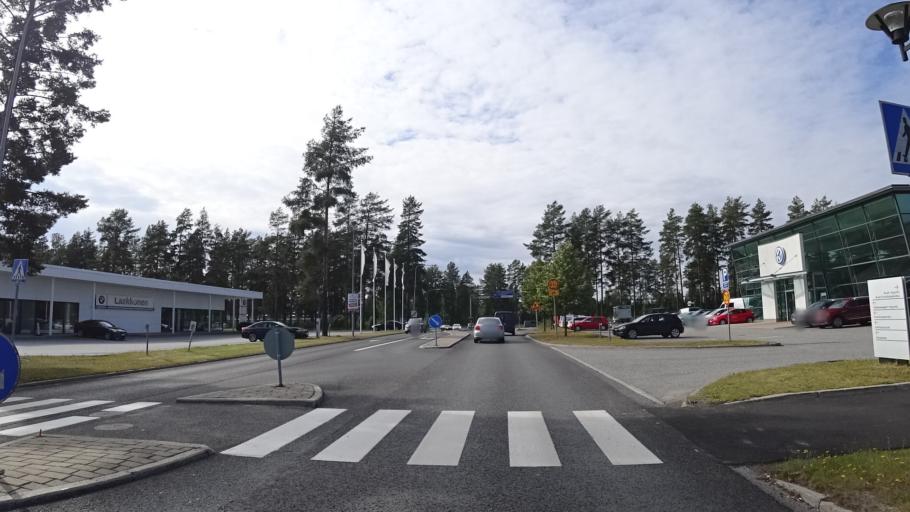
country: FI
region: North Karelia
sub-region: Joensuu
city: Joensuu
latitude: 62.6197
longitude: 29.7774
